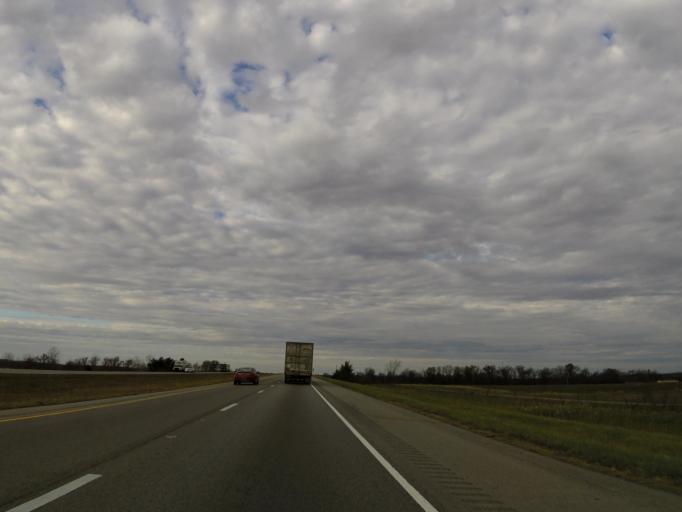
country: US
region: Illinois
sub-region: Clinton County
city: Wamac
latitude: 38.3624
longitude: -89.0658
